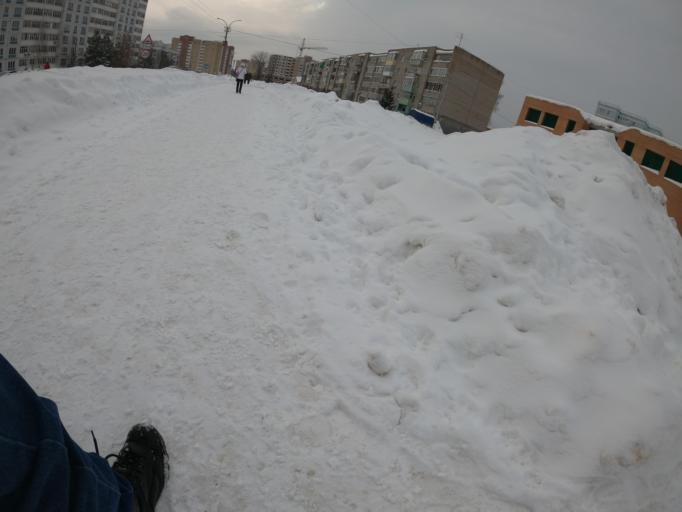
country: RU
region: Moskovskaya
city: Elektrogorsk
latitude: 55.8864
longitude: 38.7743
